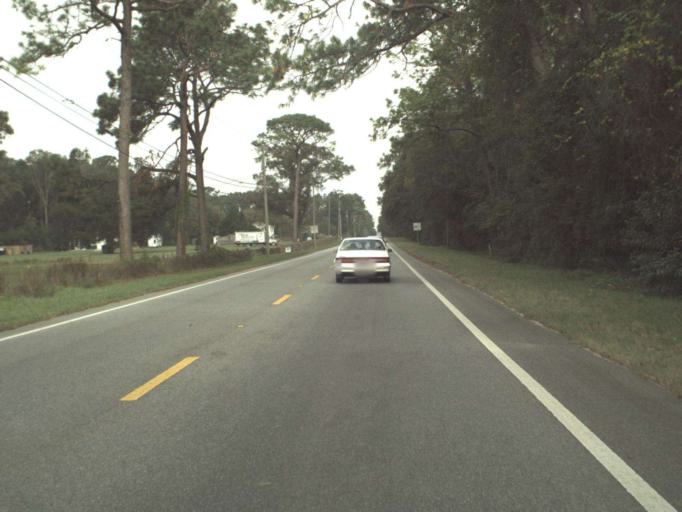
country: US
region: Florida
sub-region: Leon County
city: Woodville
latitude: 30.2913
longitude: -84.2426
